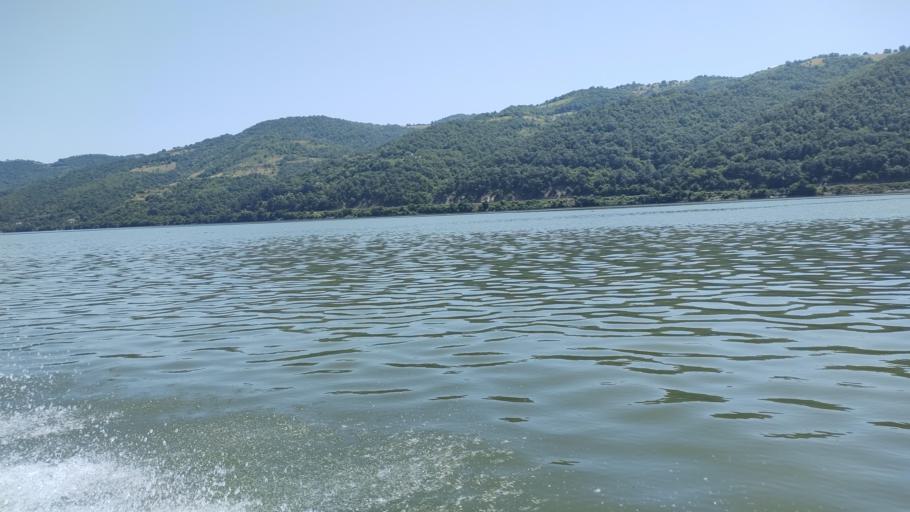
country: RO
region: Mehedinti
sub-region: Comuna Svinita
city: Svinita
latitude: 44.5110
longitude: 22.1959
